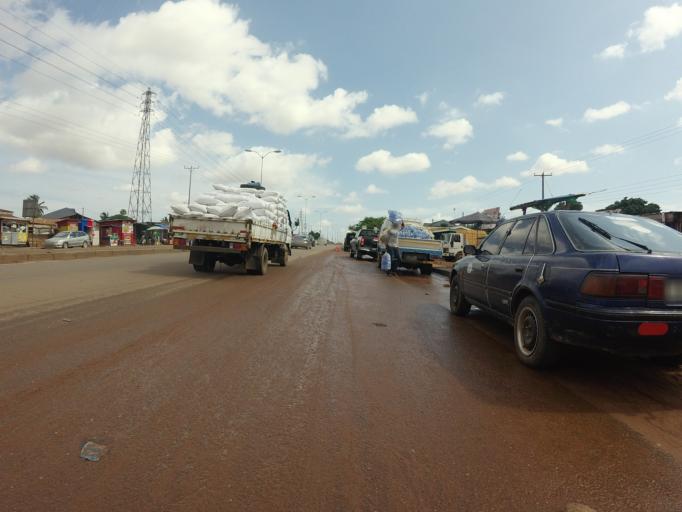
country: GH
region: Greater Accra
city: Medina Estates
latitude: 5.7440
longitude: -0.1771
